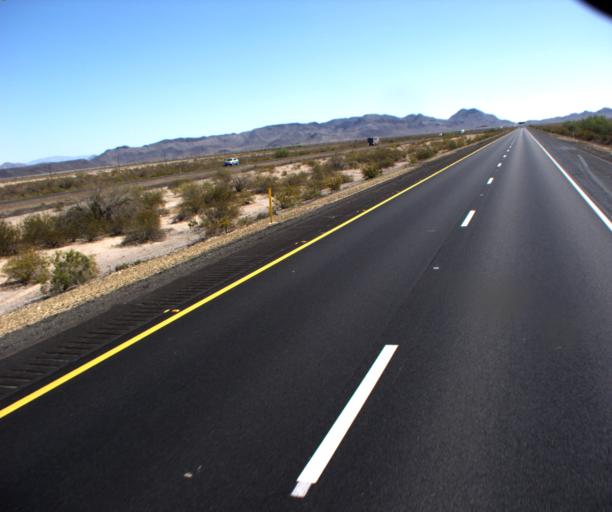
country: US
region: Arizona
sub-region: La Paz County
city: Salome
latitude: 33.6221
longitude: -113.7098
